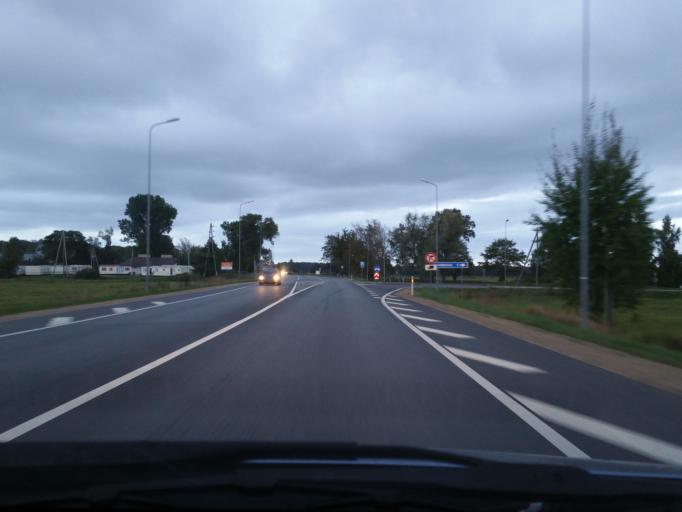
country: LV
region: Adazi
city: Adazi
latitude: 57.1015
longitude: 24.3126
